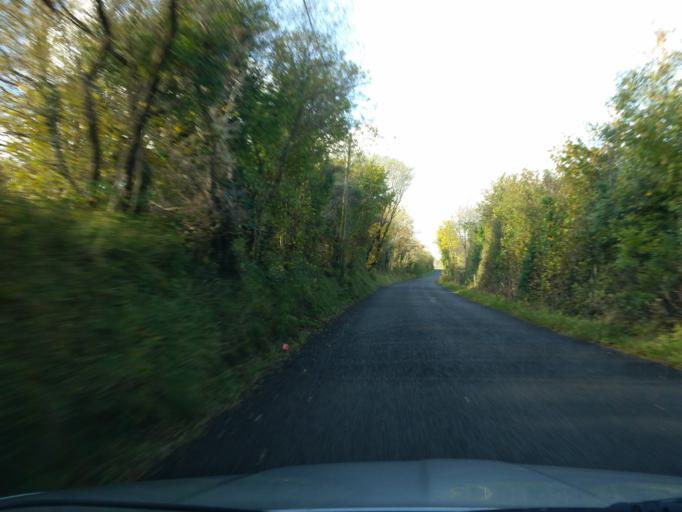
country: GB
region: Northern Ireland
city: Lisnaskea
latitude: 54.2490
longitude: -7.3899
